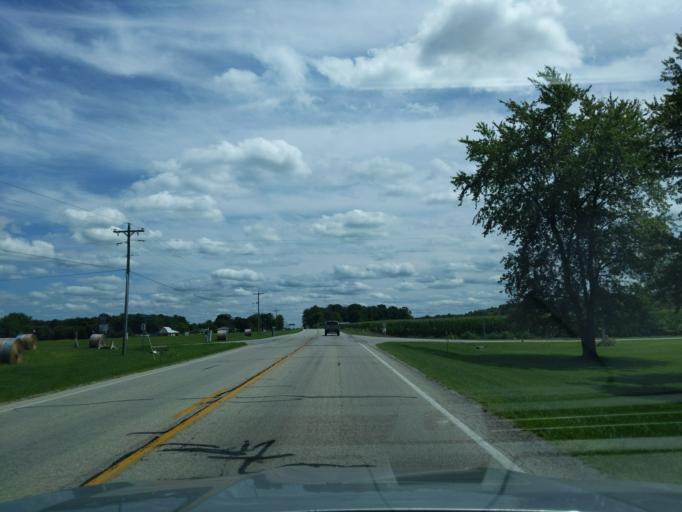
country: US
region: Indiana
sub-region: Ripley County
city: Batesville
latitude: 39.3086
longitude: -85.2939
